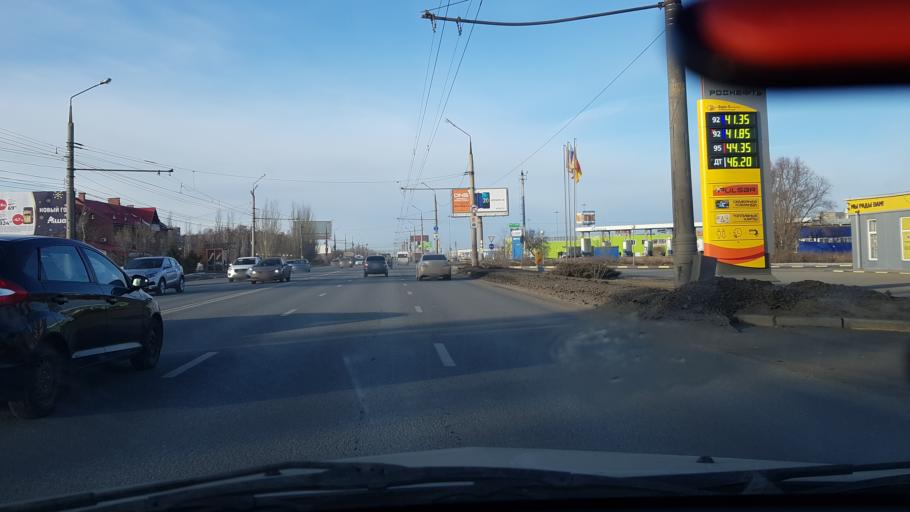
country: RU
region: Samara
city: Tol'yatti
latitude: 53.5372
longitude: 49.3923
